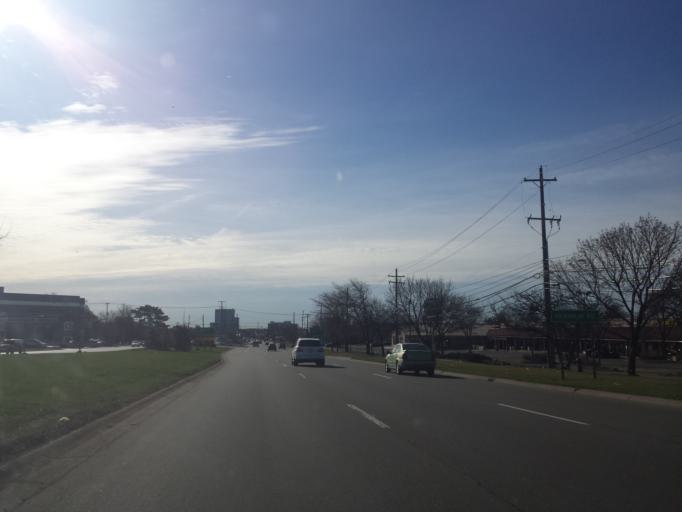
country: US
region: Michigan
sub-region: Oakland County
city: Franklin
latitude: 42.5027
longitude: -83.3121
